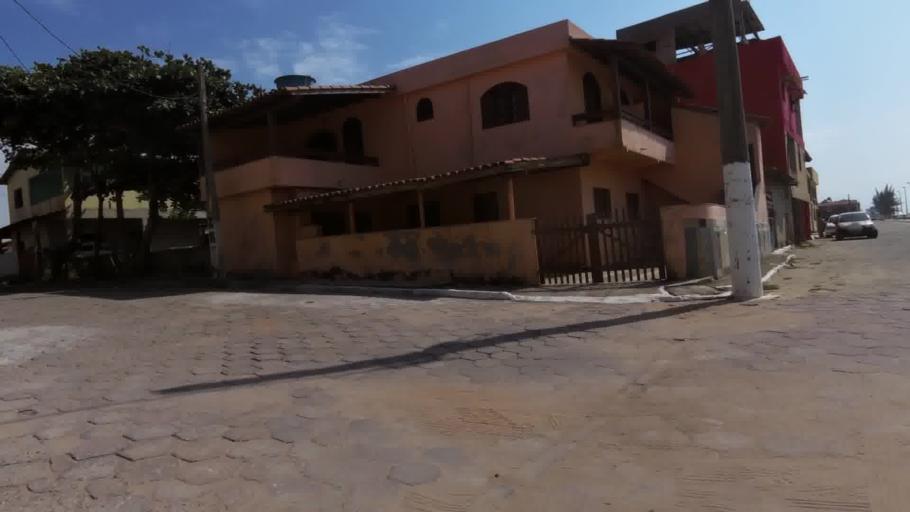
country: BR
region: Espirito Santo
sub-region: Marataizes
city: Marataizes
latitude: -21.0315
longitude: -40.8129
